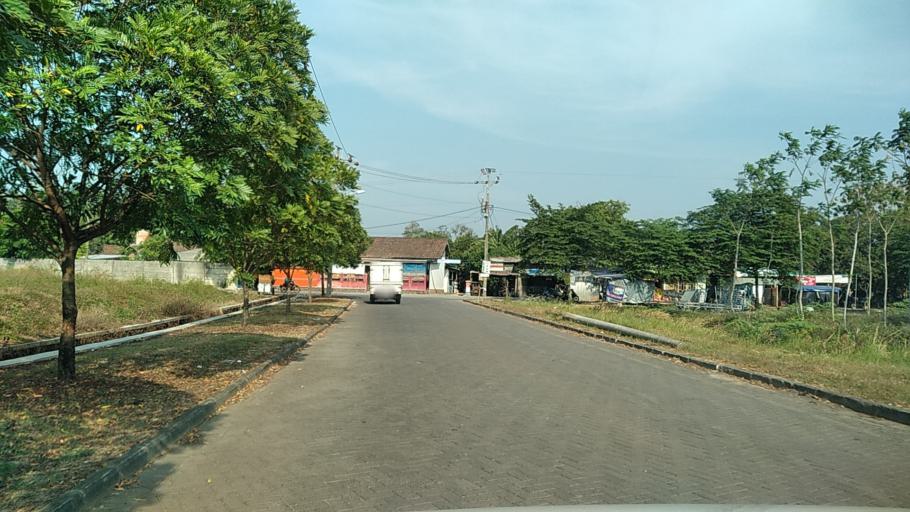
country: ID
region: Central Java
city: Semarang
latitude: -7.0524
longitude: 110.3258
